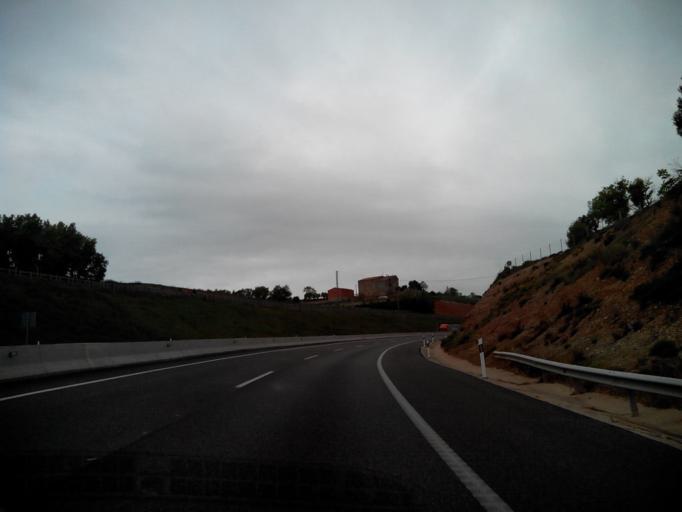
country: ES
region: Catalonia
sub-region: Provincia de Barcelona
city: Calaf
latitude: 41.7325
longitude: 1.5605
